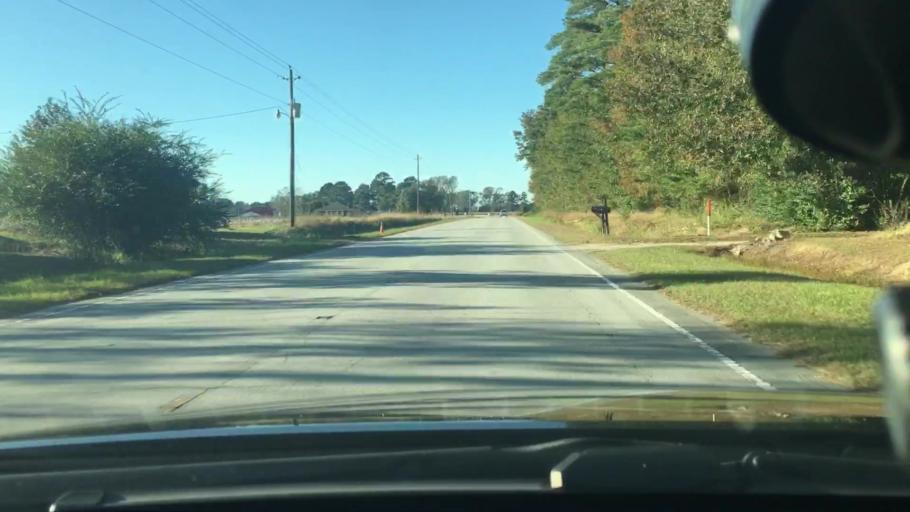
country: US
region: North Carolina
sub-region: Craven County
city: Vanceboro
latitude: 35.3702
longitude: -77.2064
